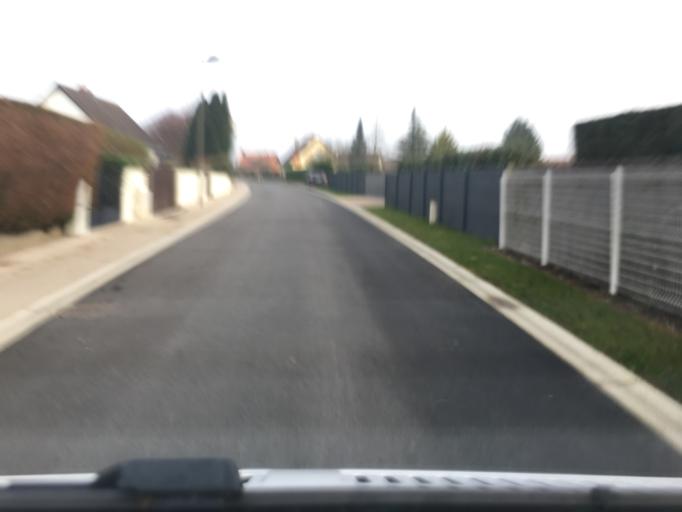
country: FR
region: Picardie
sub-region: Departement de la Somme
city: Saint-Valery-sur-Somme
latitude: 50.1786
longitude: 1.6308
